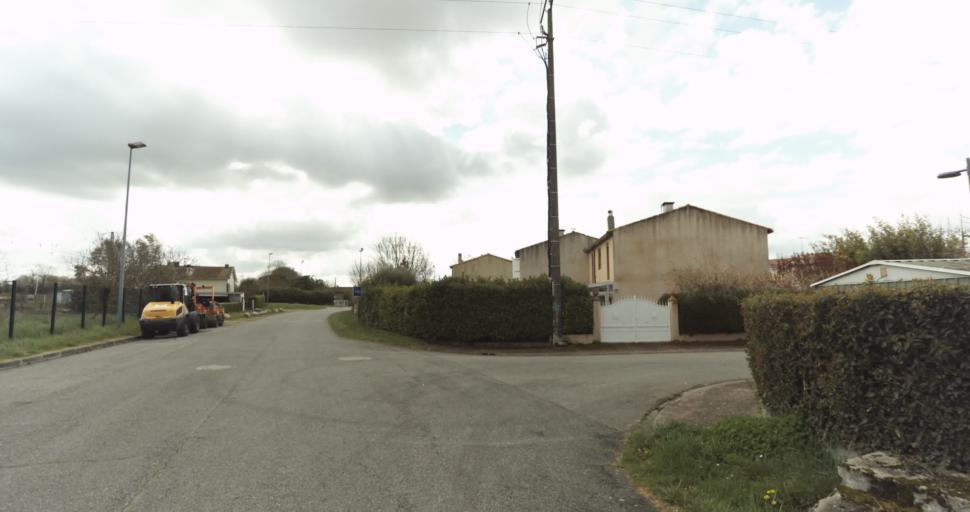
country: FR
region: Midi-Pyrenees
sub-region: Departement de la Haute-Garonne
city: Auterive
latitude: 43.3467
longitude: 1.4701
